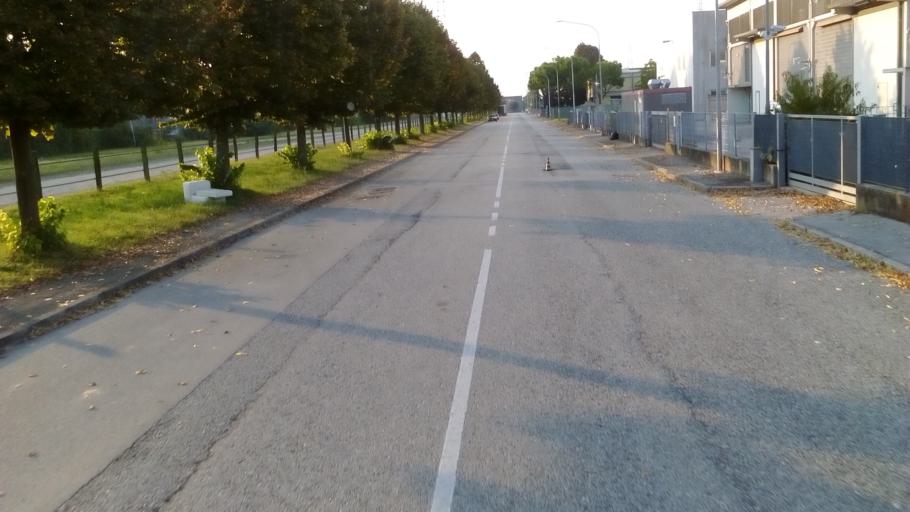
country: IT
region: Veneto
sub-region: Provincia di Padova
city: Villatora
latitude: 45.3801
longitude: 11.9643
